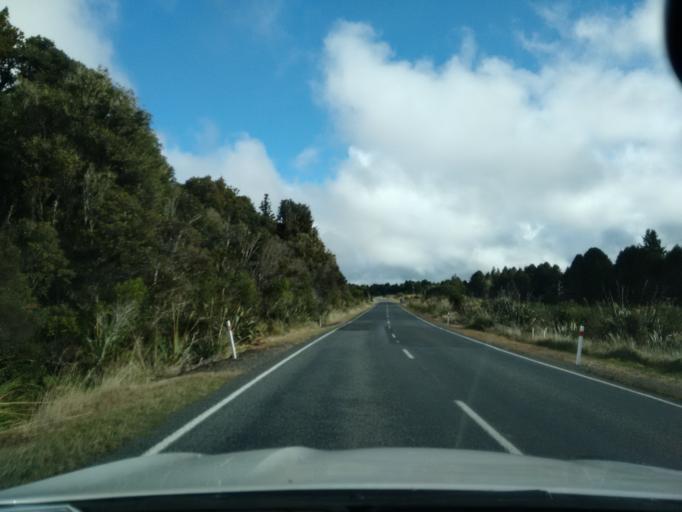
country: NZ
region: Manawatu-Wanganui
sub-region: Ruapehu District
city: Waiouru
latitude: -39.2438
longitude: 175.3913
